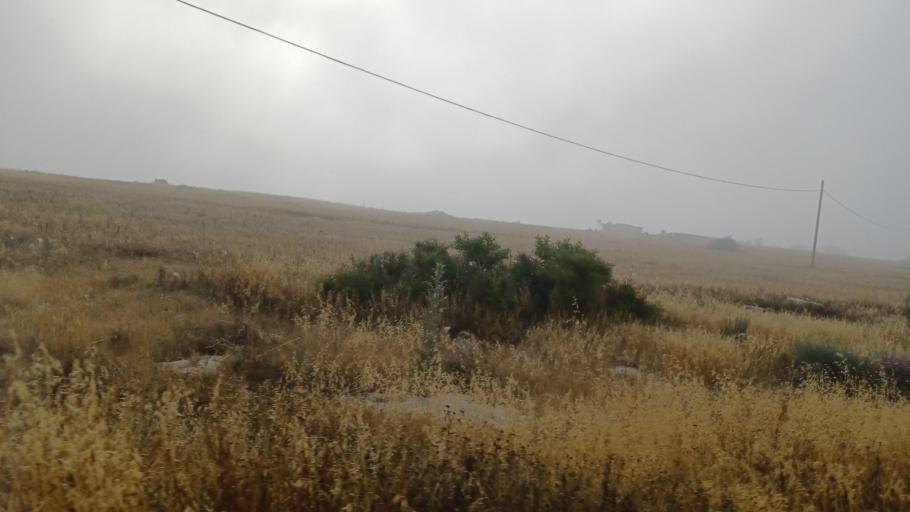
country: CY
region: Ammochostos
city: Acheritou
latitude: 35.0993
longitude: 33.8772
